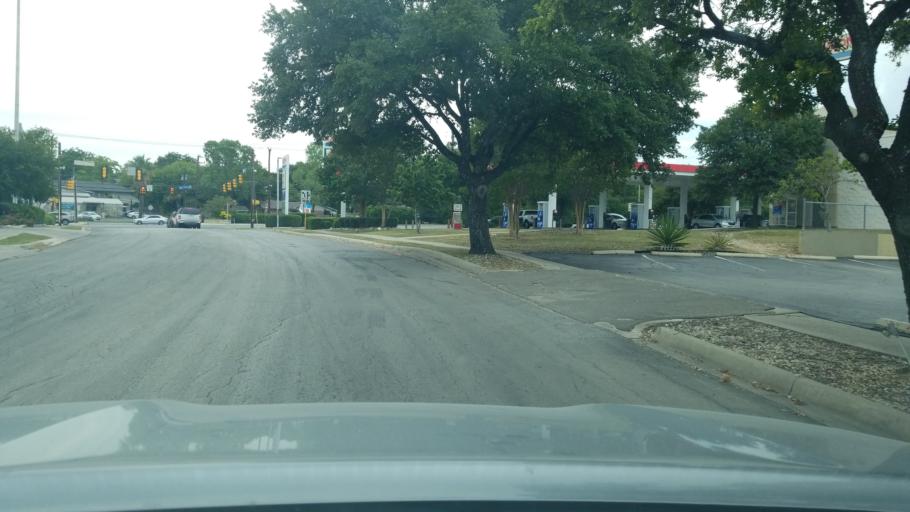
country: US
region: Texas
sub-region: Bexar County
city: Castle Hills
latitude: 29.5325
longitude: -98.4950
